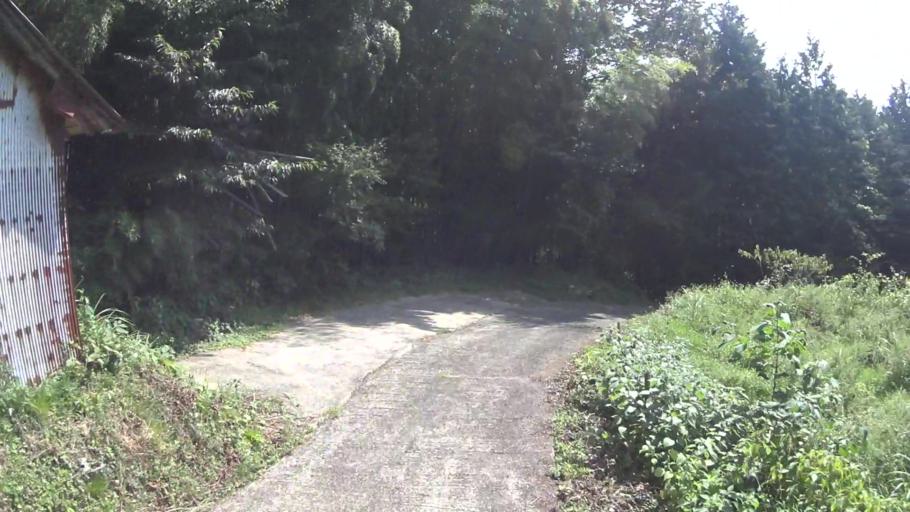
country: JP
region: Kyoto
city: Miyazu
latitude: 35.6842
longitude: 135.2331
